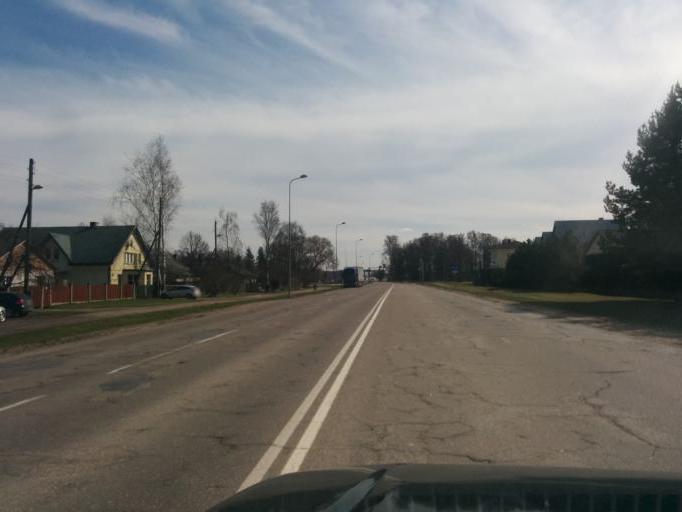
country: LV
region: Jelgava
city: Jelgava
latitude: 56.6435
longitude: 23.6944
